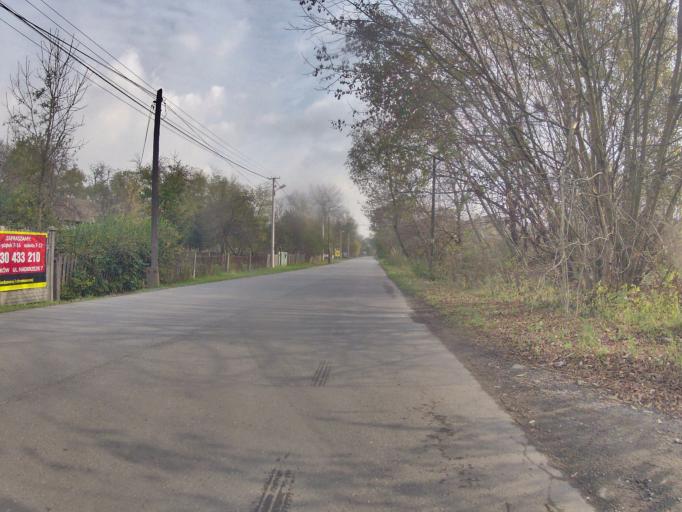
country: PL
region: Lesser Poland Voivodeship
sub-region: Powiat wielicki
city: Wegrzce Wielkie
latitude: 50.0699
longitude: 20.1039
